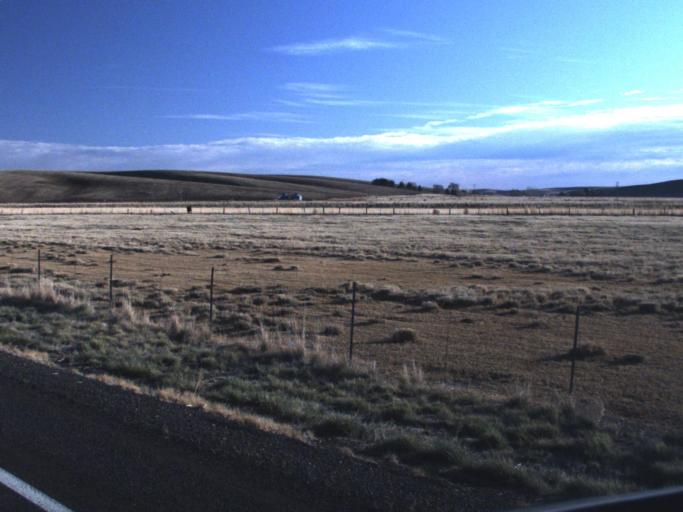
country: US
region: Washington
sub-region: Garfield County
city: Pomeroy
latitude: 46.7715
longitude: -117.7065
